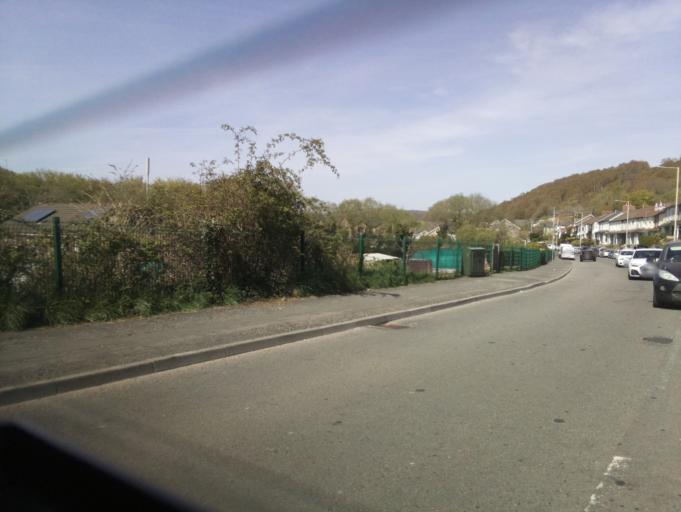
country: GB
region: Wales
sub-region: Rhondda Cynon Taf
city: Pontypridd
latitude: 51.6089
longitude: -3.3276
